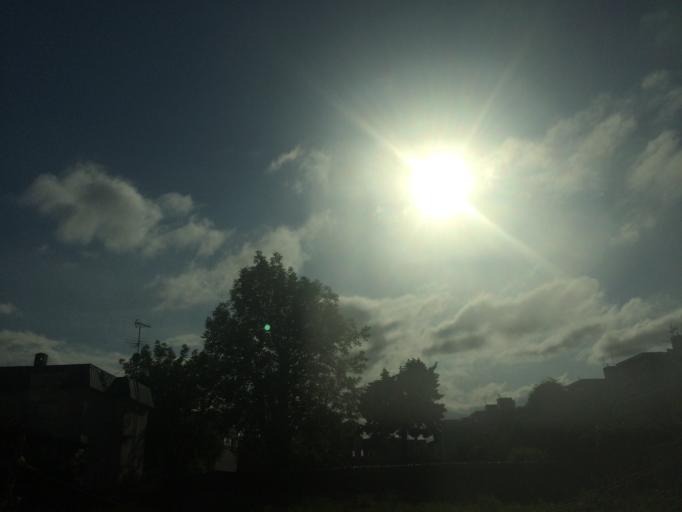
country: JP
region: Hokkaido
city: Sapporo
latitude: 43.0403
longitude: 141.3508
